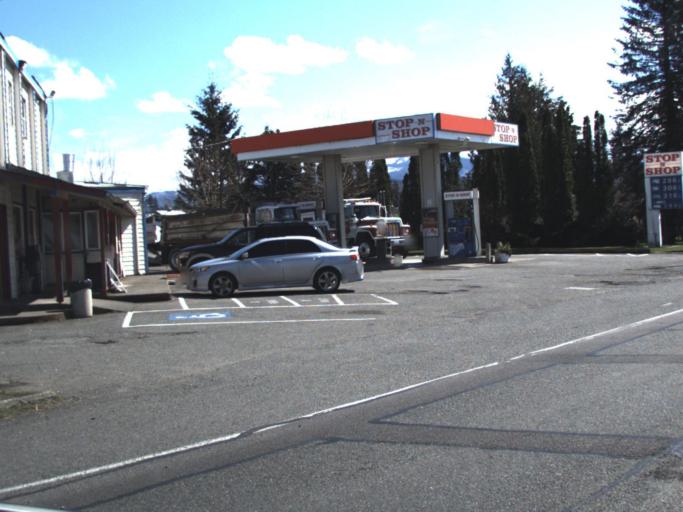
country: US
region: Washington
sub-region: King County
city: Enumclaw
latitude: 47.2284
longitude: -121.9897
